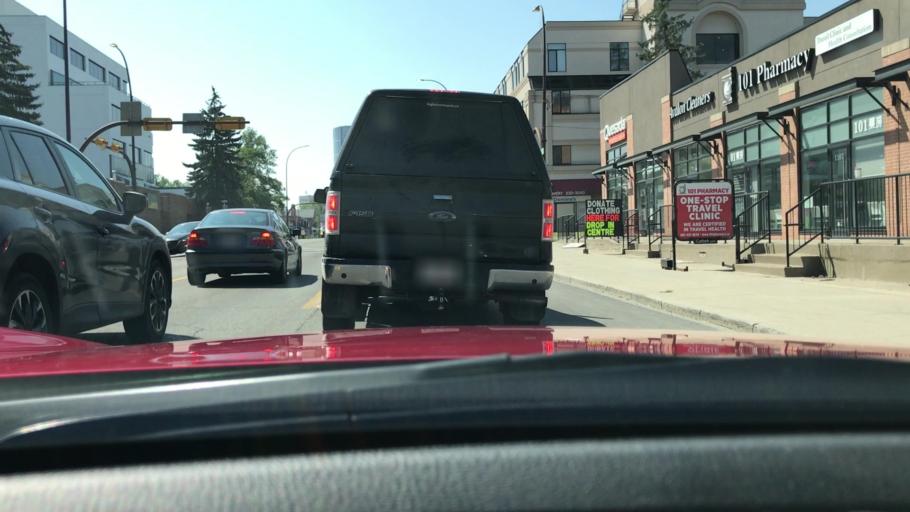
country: CA
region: Alberta
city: Calgary
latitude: 51.0620
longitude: -114.0626
